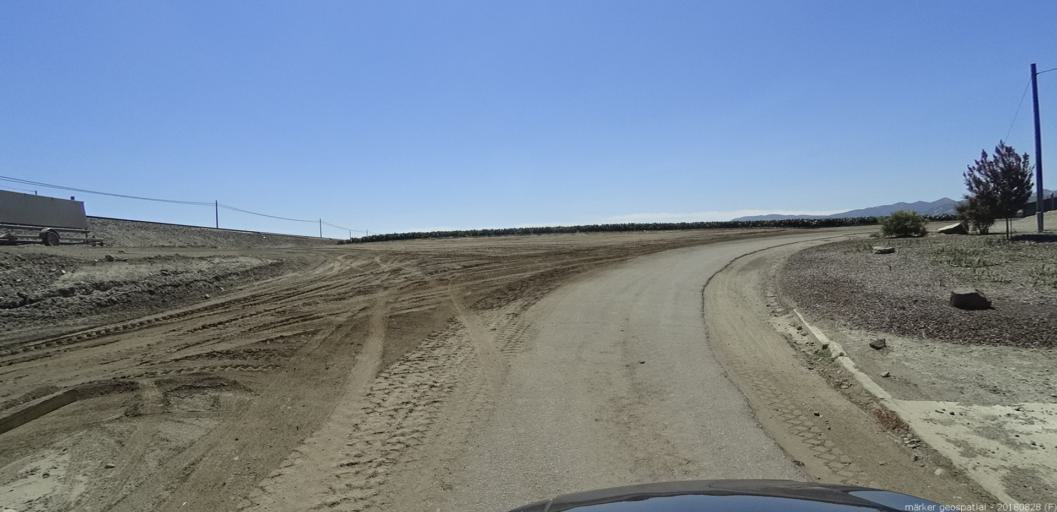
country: US
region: California
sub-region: San Luis Obispo County
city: Lake Nacimiento
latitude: 36.0171
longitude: -120.8989
